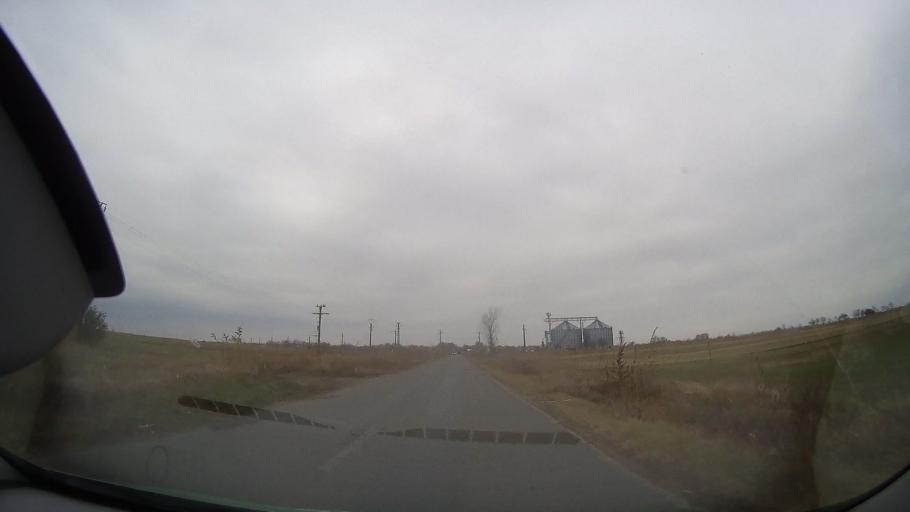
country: RO
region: Buzau
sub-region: Comuna Luciu
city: Luciu
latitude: 44.9672
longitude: 27.1008
